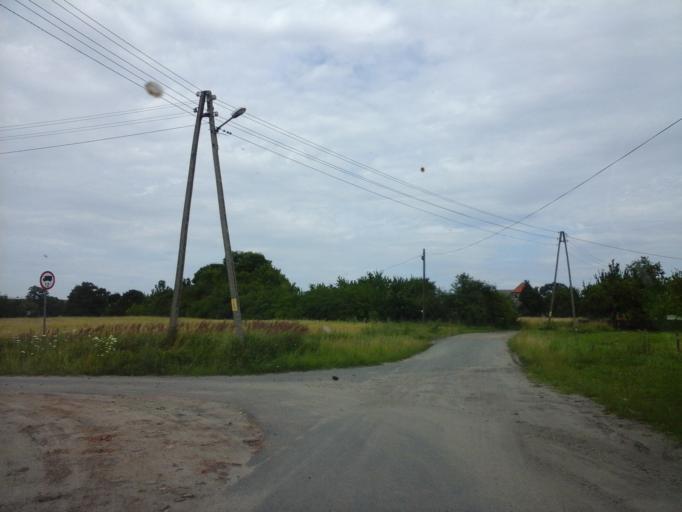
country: PL
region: Lubusz
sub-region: Powiat strzelecko-drezdenecki
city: Dobiegniew
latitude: 53.0487
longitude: 15.7595
